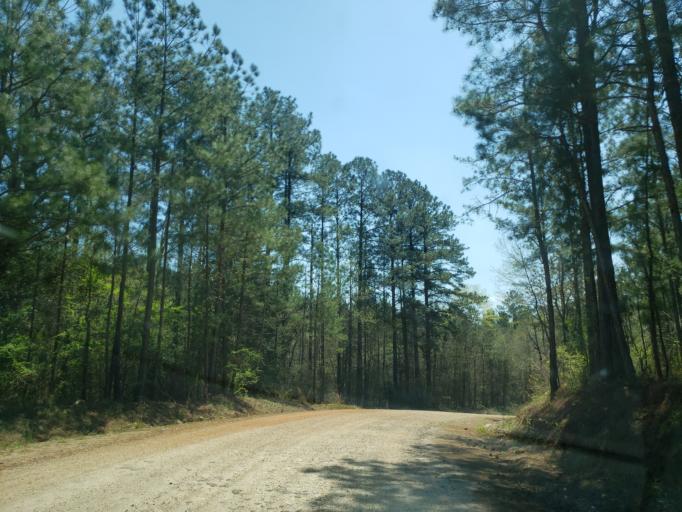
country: US
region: Alabama
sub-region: Tallapoosa County
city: Camp Hill
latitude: 32.6762
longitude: -85.6628
